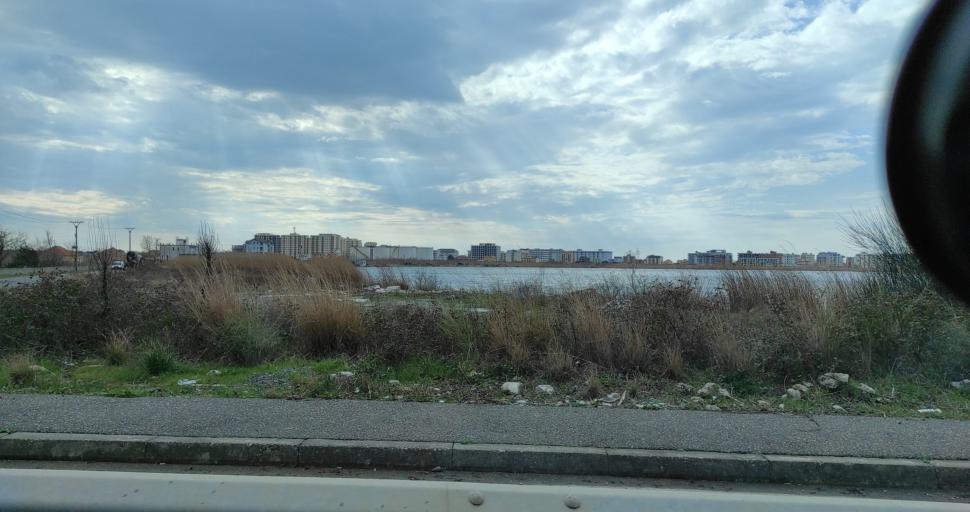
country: AL
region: Lezhe
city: Shengjin
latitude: 41.8013
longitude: 19.6161
